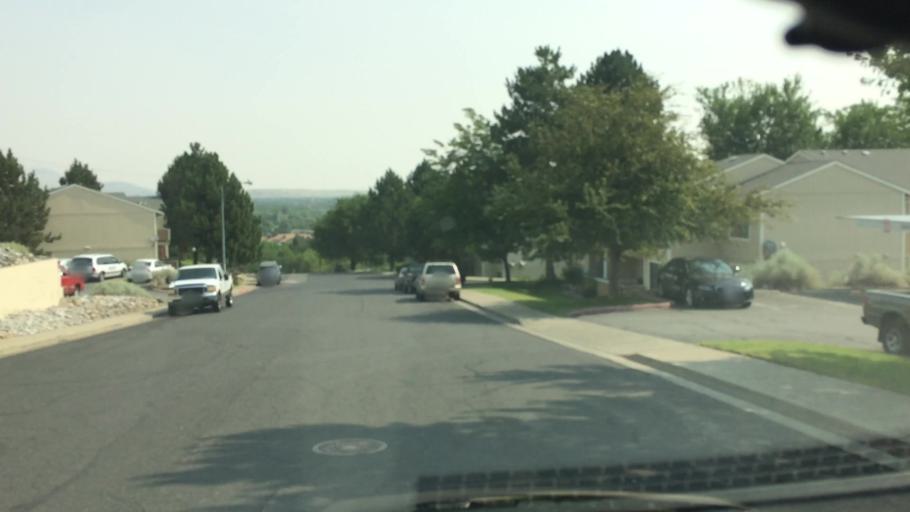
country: US
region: Nevada
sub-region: Washoe County
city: Sun Valley
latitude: 39.5665
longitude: -119.7840
